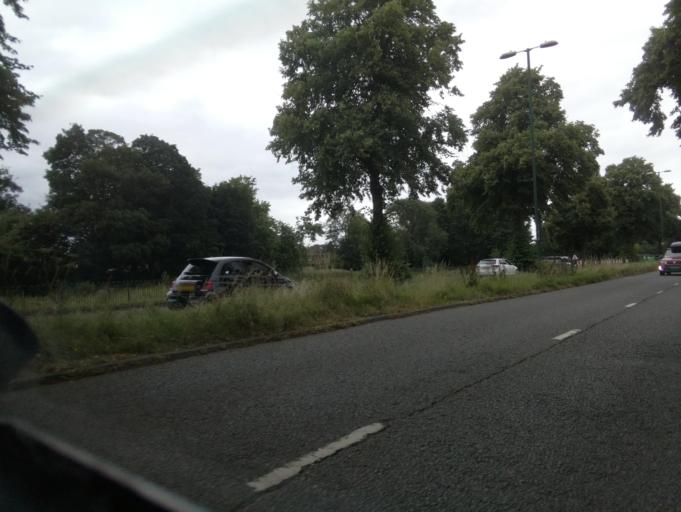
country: GB
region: England
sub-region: Nottinghamshire
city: Arnold
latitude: 52.9899
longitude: -1.1472
